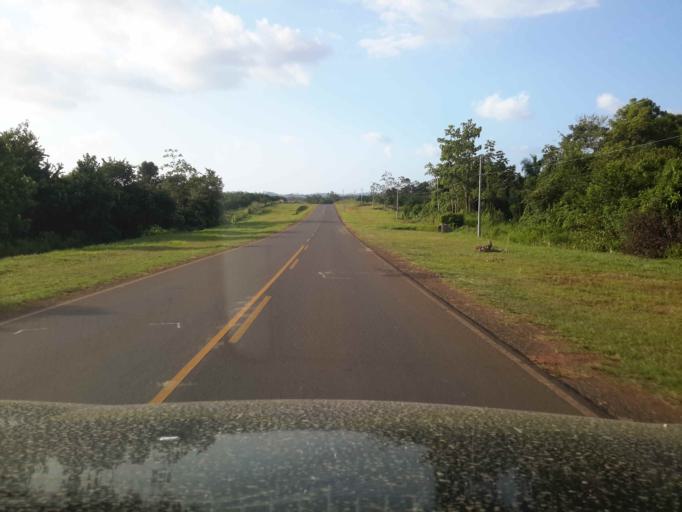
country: NI
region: Rio San Juan
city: San Carlos
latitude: 11.1632
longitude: -84.6629
